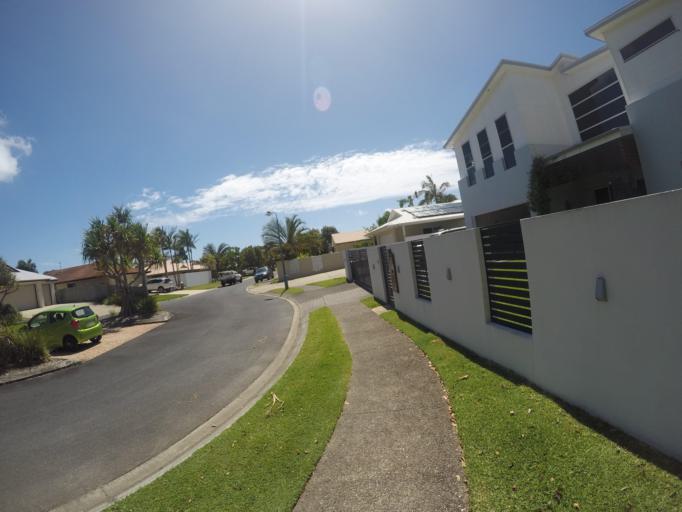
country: AU
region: Queensland
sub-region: Sunshine Coast
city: Mooloolaba
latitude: -26.6138
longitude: 153.0935
